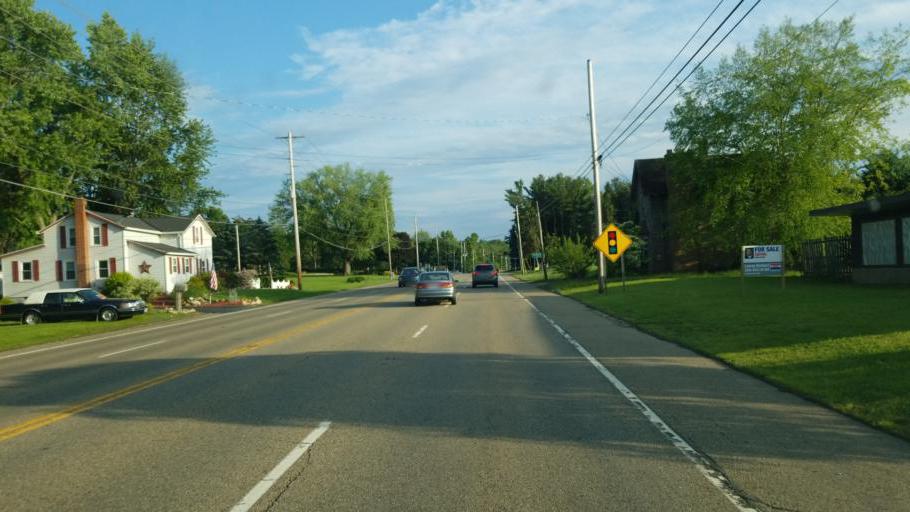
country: US
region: Ohio
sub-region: Stark County
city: Uniontown
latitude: 40.9903
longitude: -81.4057
